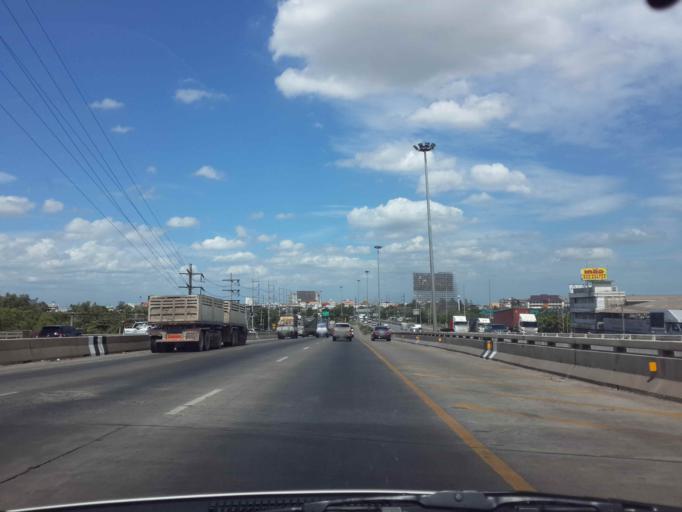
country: TH
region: Samut Sakhon
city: Samut Sakhon
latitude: 13.5442
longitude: 100.2513
